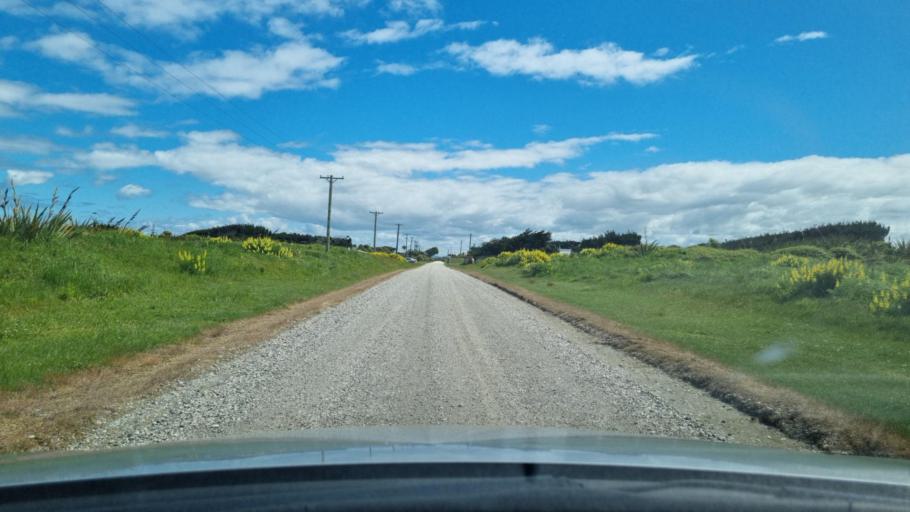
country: NZ
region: Southland
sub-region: Invercargill City
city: Invercargill
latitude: -46.4329
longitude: 168.2354
